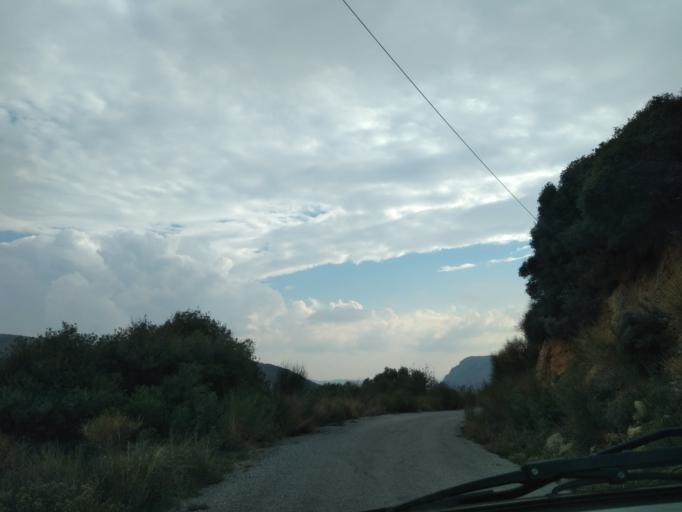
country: GR
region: Crete
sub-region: Nomos Lasithiou
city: Makry-Gialos
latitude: 35.1233
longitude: 26.0219
